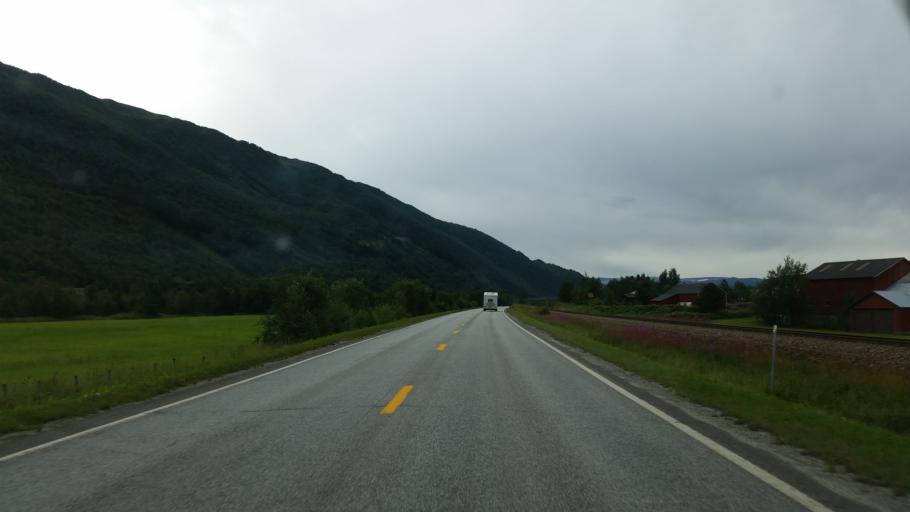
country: NO
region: Nordland
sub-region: Saltdal
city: Rognan
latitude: 67.0509
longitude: 15.3853
